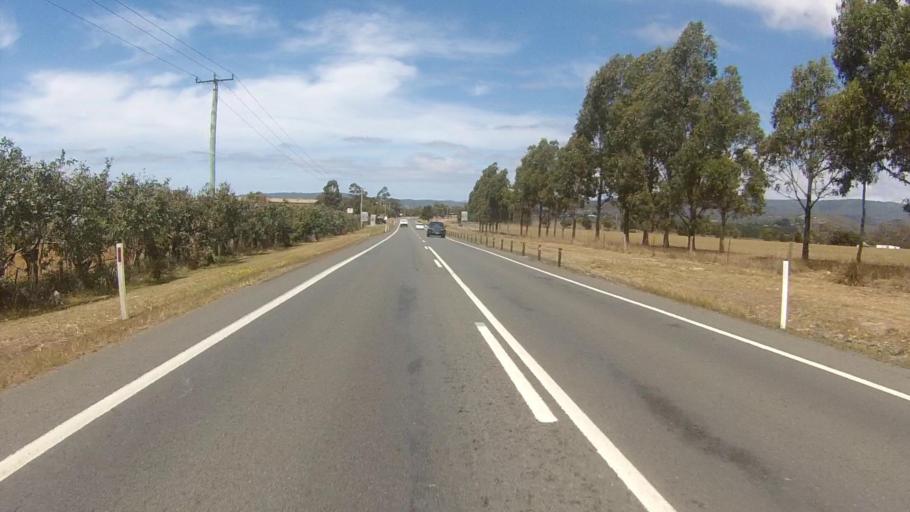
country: AU
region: Tasmania
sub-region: Kingborough
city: Margate
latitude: -43.0115
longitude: 147.2720
